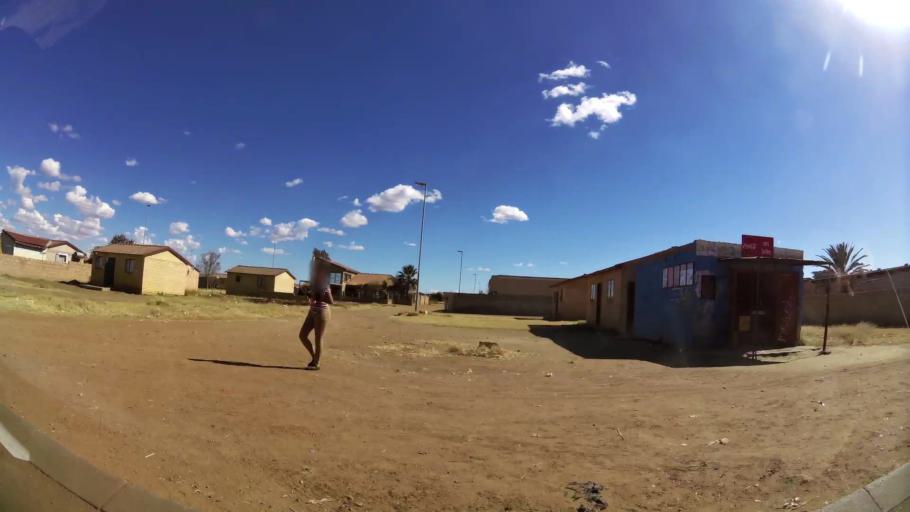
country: ZA
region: North-West
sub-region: Dr Kenneth Kaunda District Municipality
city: Klerksdorp
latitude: -26.8718
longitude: 26.5748
